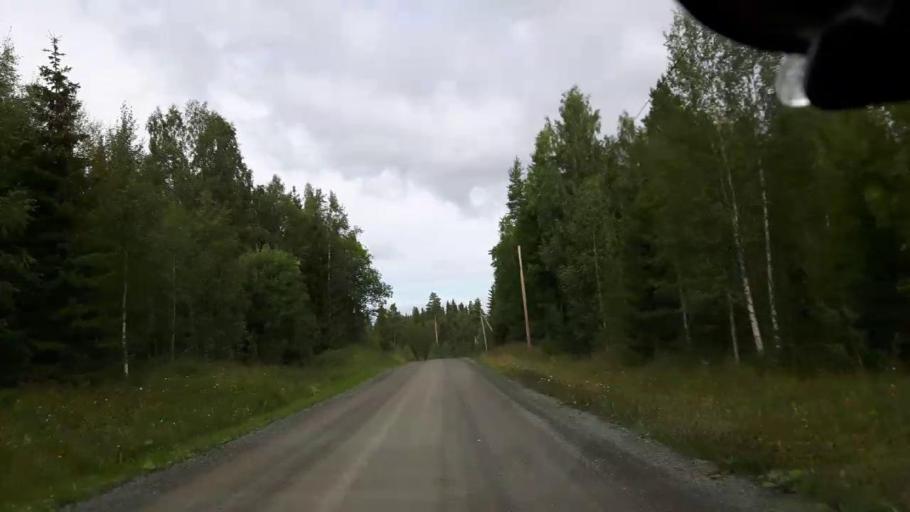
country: SE
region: Jaemtland
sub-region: Krokoms Kommun
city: Valla
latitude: 63.4009
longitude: 14.0955
